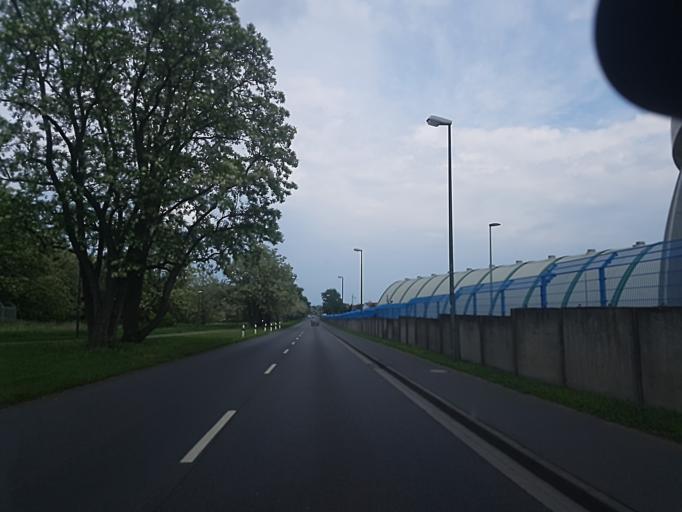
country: DE
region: Saxony-Anhalt
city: Wittenburg
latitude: 51.8801
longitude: 12.5873
